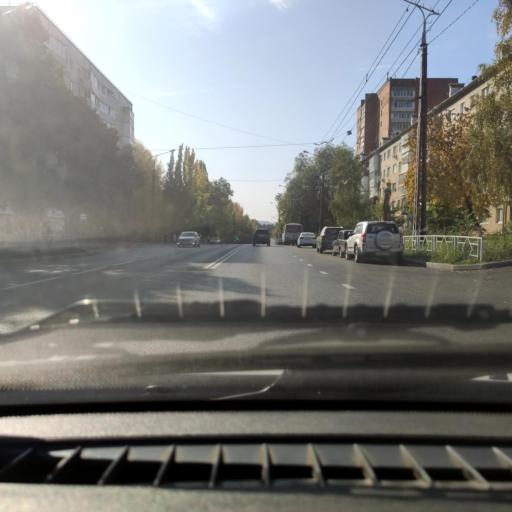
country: RU
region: Samara
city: Zhigulevsk
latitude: 53.4825
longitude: 49.4600
